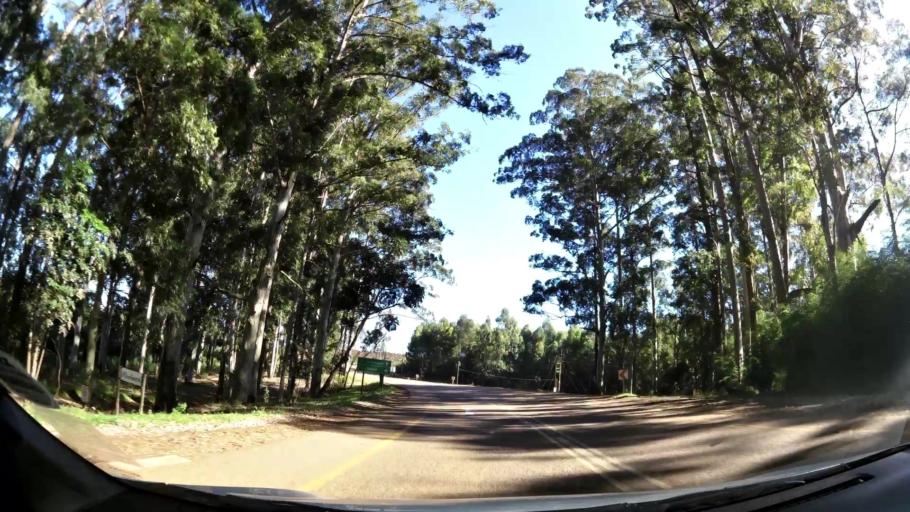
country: ZA
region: Limpopo
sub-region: Capricorn District Municipality
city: Mankoeng
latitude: -23.9151
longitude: 29.9612
